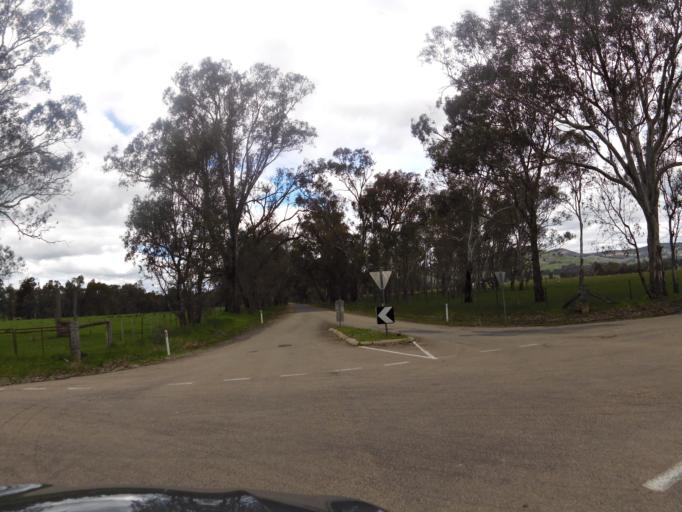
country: AU
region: Victoria
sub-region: Benalla
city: Benalla
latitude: -36.6644
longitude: 145.9175
